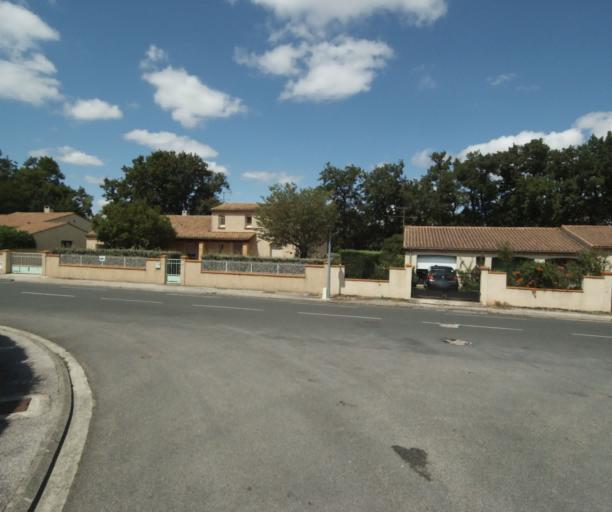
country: FR
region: Midi-Pyrenees
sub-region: Departement de la Haute-Garonne
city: Revel
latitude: 43.4512
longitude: 2.0064
